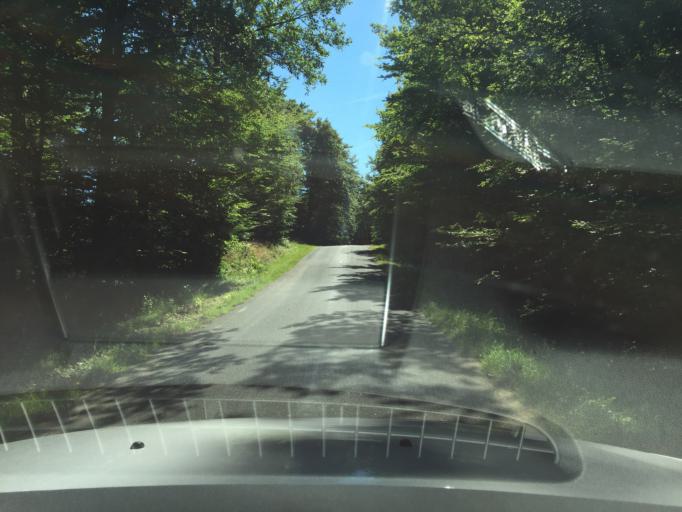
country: SE
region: Skane
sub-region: Hassleholms Kommun
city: Sosdala
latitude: 56.0152
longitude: 13.5972
